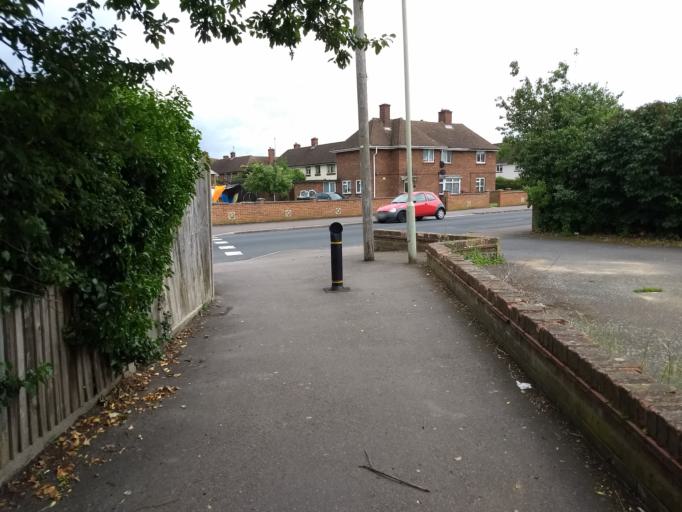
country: GB
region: England
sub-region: Bedford
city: Kempston
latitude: 52.1140
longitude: -0.5019
